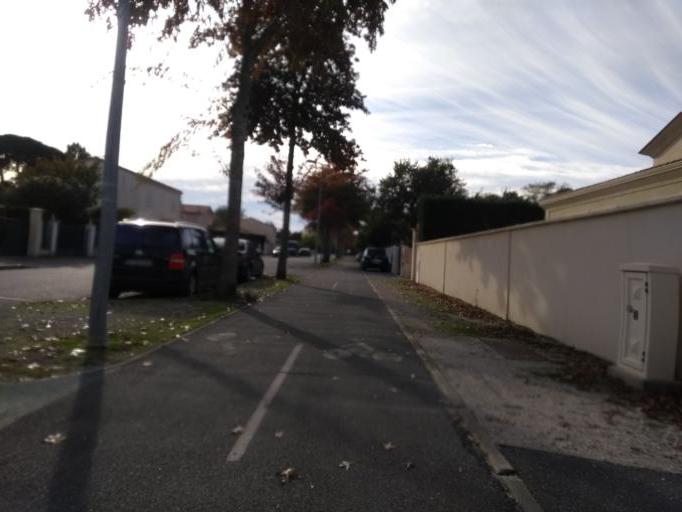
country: FR
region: Aquitaine
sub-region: Departement de la Gironde
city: Pessac
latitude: 44.7986
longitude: -0.6821
